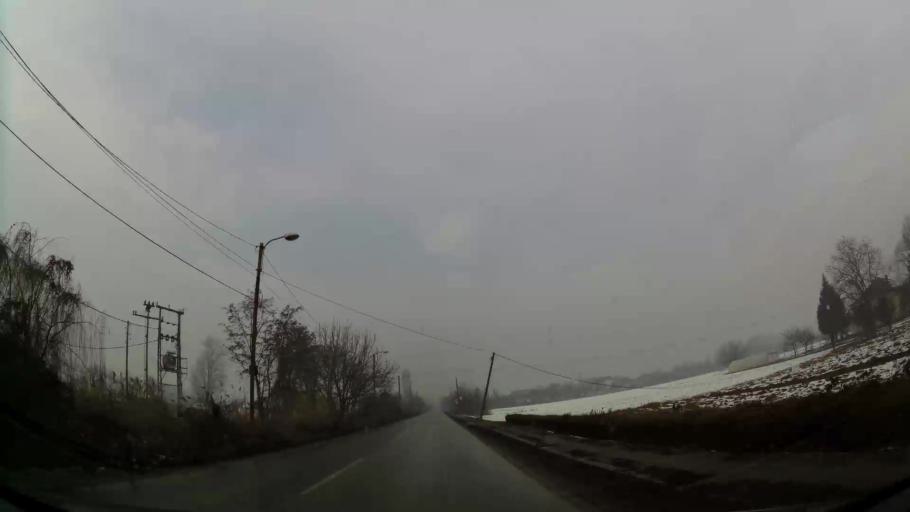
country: MK
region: Ilinden
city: Jurumleri
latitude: 41.9674
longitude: 21.5495
